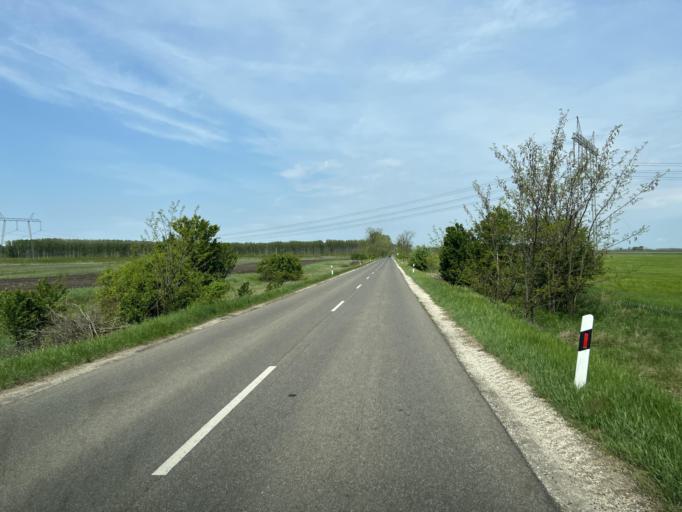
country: HU
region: Pest
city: Ujszilvas
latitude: 47.2326
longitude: 19.9631
